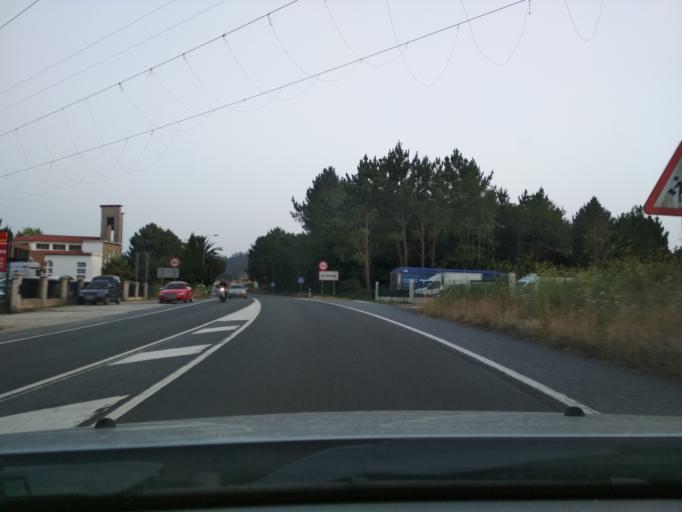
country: ES
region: Galicia
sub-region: Provincia da Coruna
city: Culleredo
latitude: 43.2691
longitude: -8.3695
